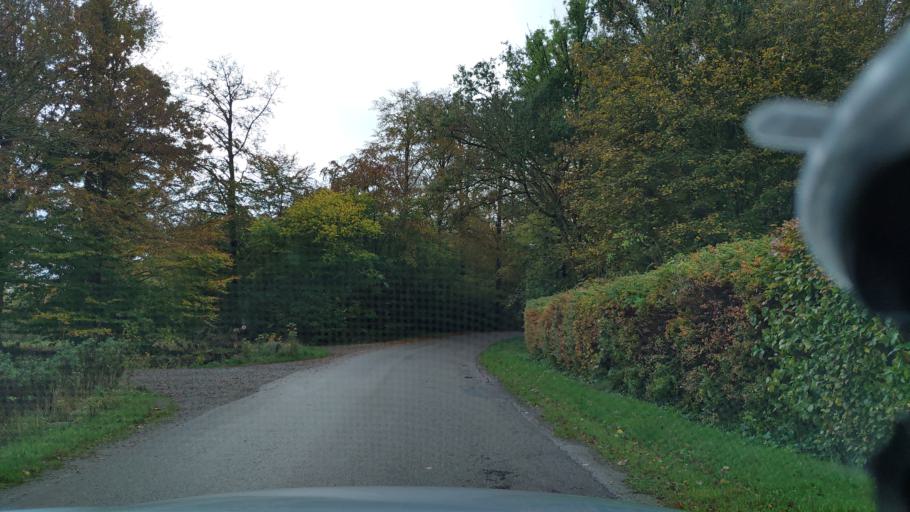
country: DK
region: Zealand
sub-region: Faxe Kommune
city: Ronnede
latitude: 55.2556
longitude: 11.9609
